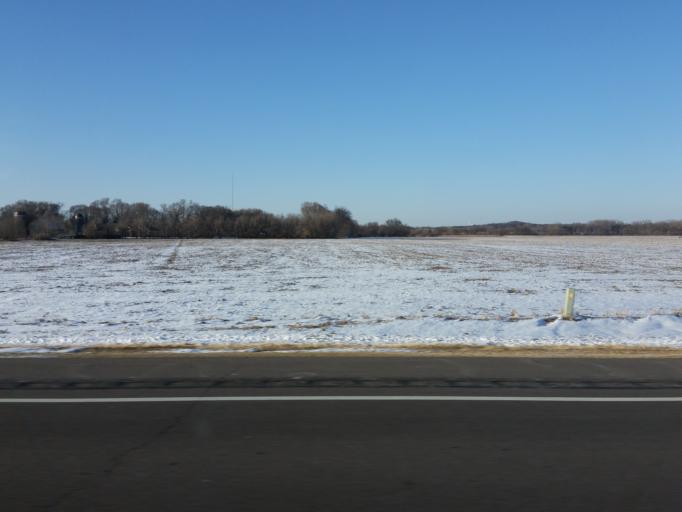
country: US
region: Minnesota
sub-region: Dakota County
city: Farmington
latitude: 44.6594
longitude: -93.0679
